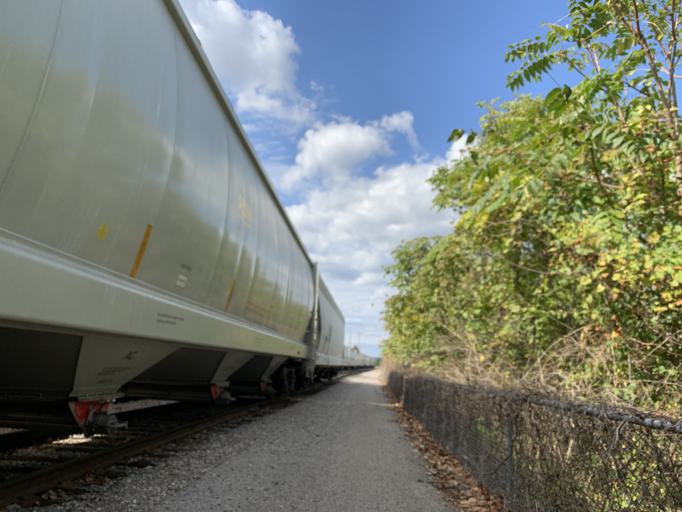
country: US
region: Kentucky
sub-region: Jefferson County
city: Louisville
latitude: 38.2683
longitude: -85.7775
